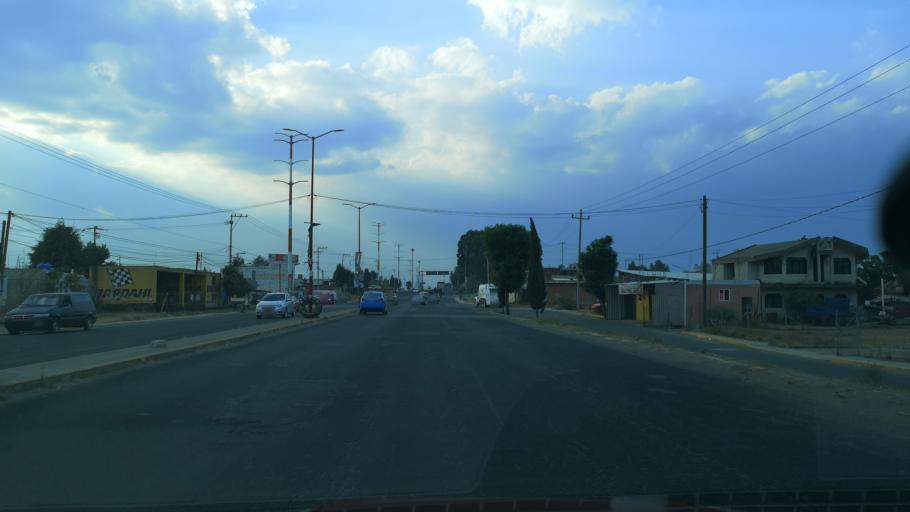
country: MX
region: Puebla
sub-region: Juan C. Bonilla
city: Santa Maria Zacatepec
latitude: 19.1270
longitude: -98.3689
